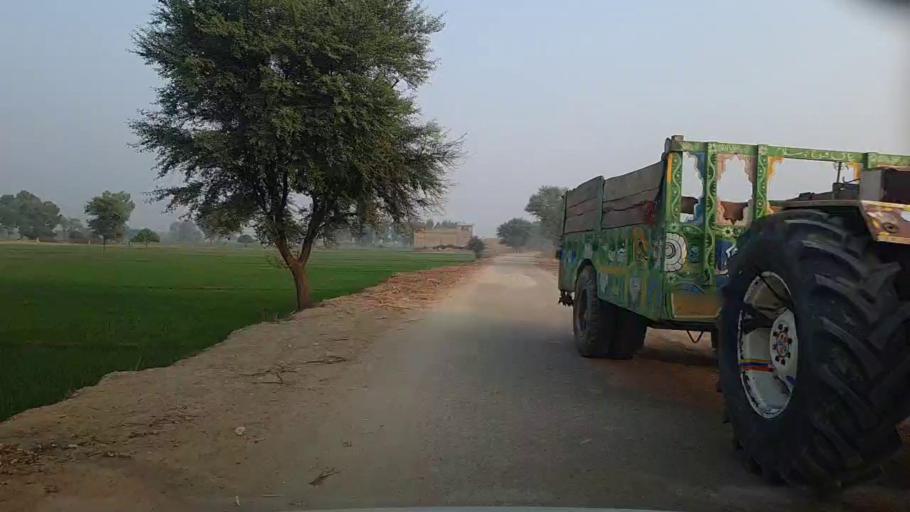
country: PK
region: Sindh
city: Bozdar
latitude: 27.0780
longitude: 68.5804
